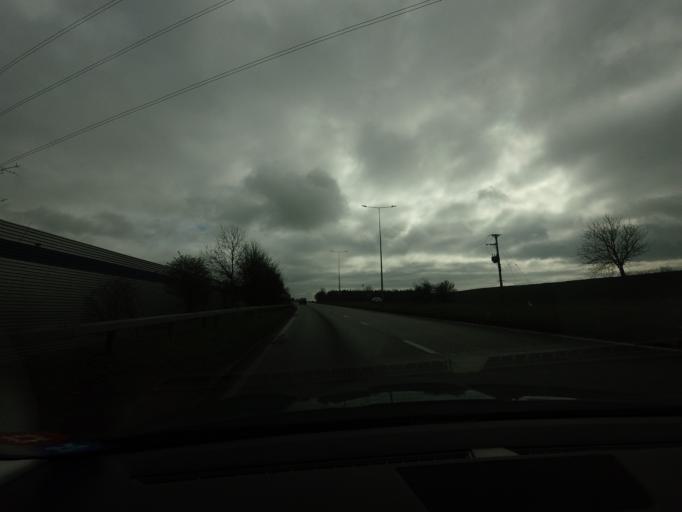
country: GB
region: England
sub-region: Kent
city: Eynsford
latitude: 51.3860
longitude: 0.1979
